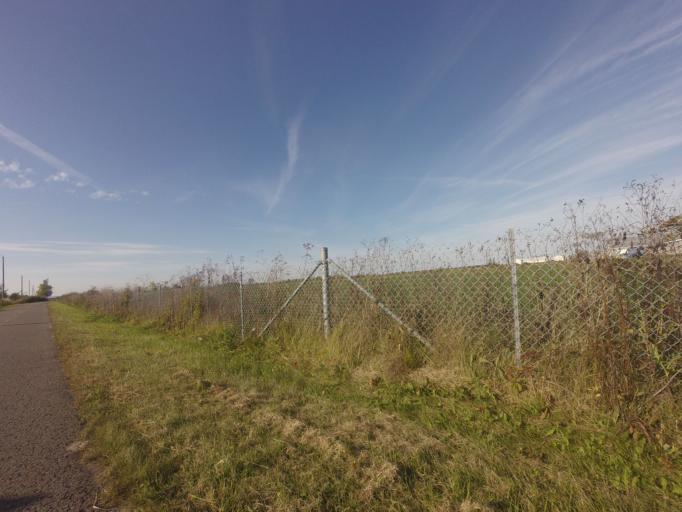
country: CA
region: Quebec
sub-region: Laurentides
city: Blainville
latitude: 45.7120
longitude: -73.9186
